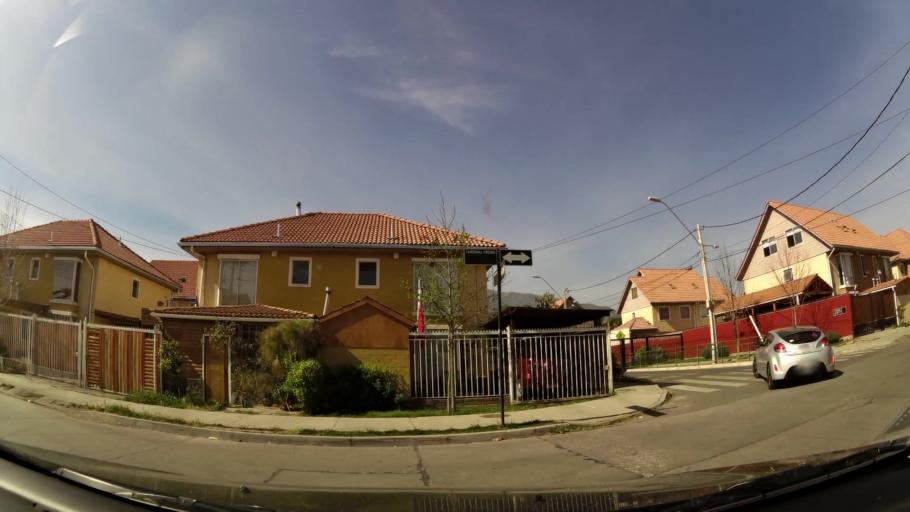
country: CL
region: Santiago Metropolitan
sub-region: Provincia de Cordillera
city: Puente Alto
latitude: -33.5927
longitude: -70.5460
